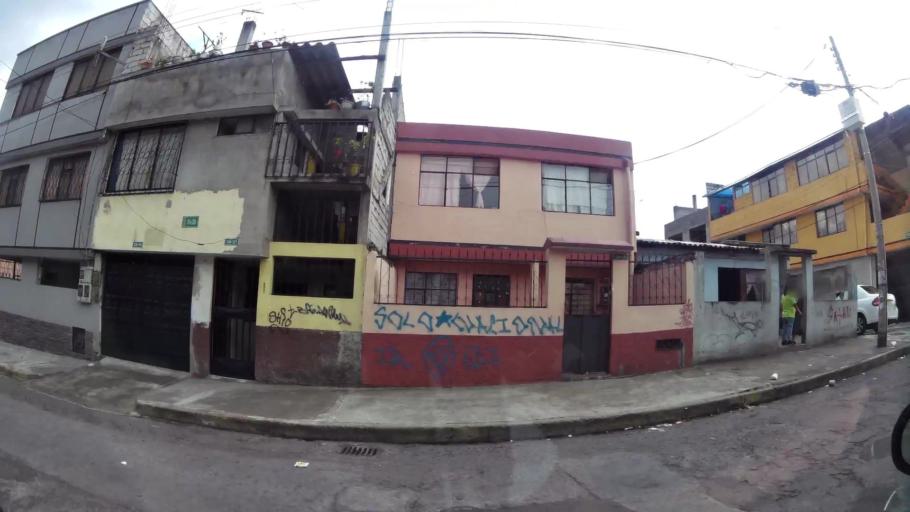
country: EC
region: Pichincha
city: Quito
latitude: -0.2843
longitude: -78.5412
